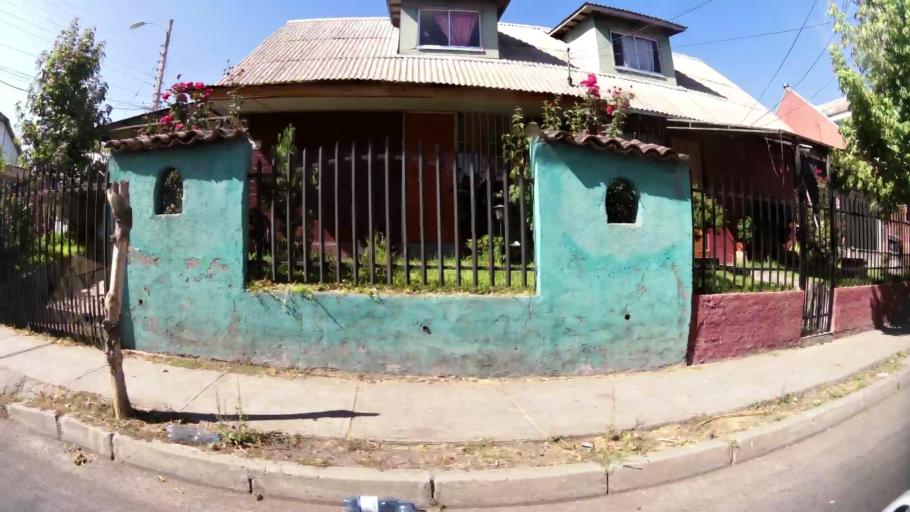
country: CL
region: Maule
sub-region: Provincia de Curico
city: Curico
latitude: -34.9779
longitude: -71.2627
